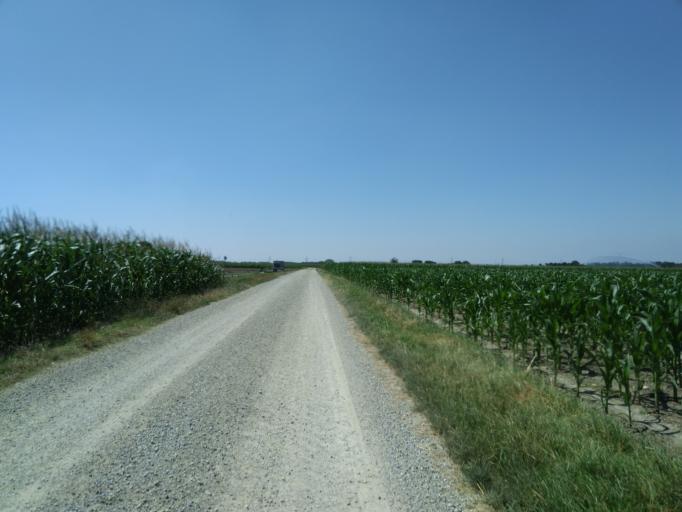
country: AT
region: Lower Austria
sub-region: Politischer Bezirk Ganserndorf
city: Deutsch-Wagram
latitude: 48.3232
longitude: 16.5679
